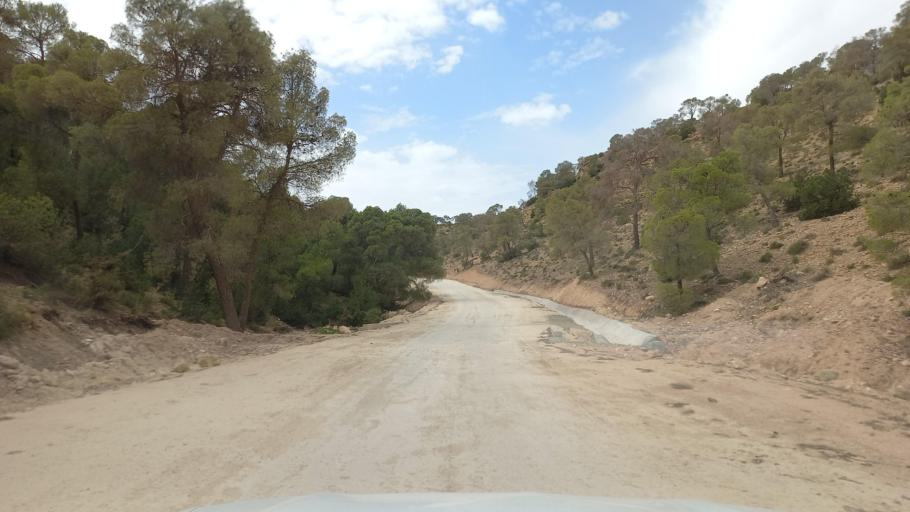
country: TN
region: Al Qasrayn
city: Kasserine
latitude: 35.3772
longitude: 8.8857
